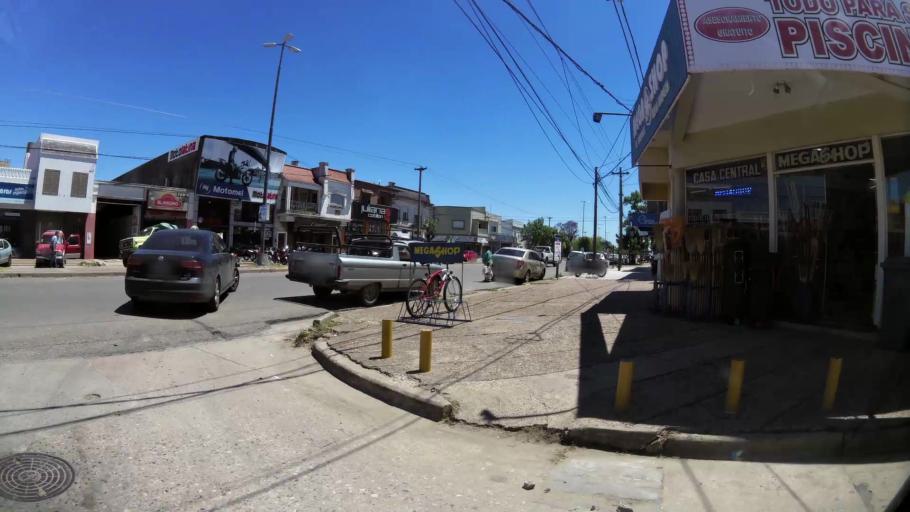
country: AR
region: Santa Fe
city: Santa Fe de la Vera Cruz
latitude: -31.6286
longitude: -60.7137
